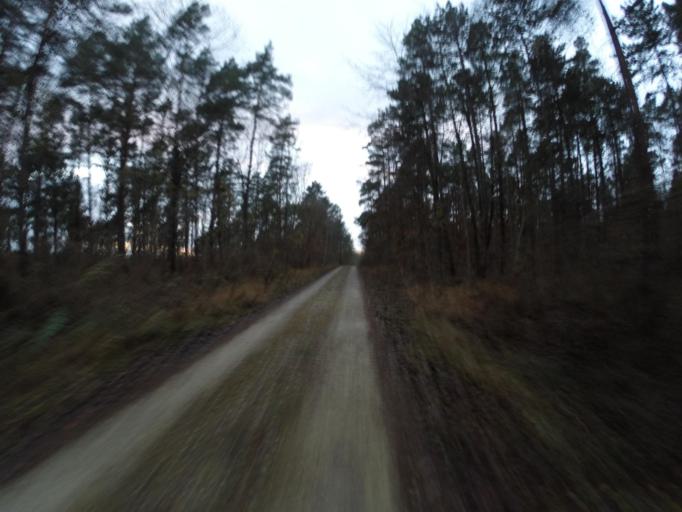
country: DE
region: Thuringia
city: Zollnitz
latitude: 50.8998
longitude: 11.6329
